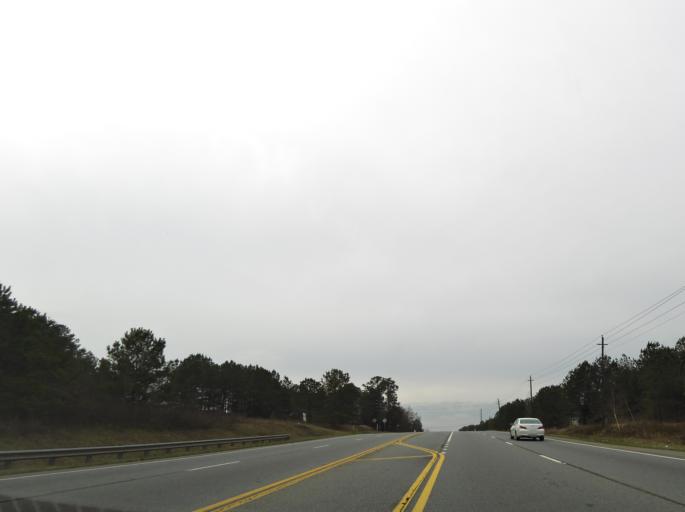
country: US
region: Georgia
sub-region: Houston County
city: Robins Air Force Base
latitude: 32.5759
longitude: -83.5901
